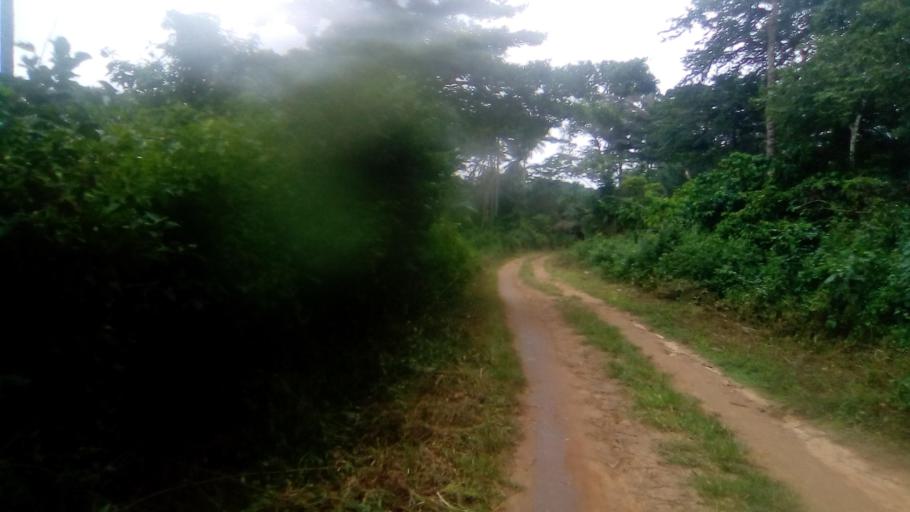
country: SL
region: Eastern Province
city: Kailahun
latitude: 8.2924
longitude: -10.5991
